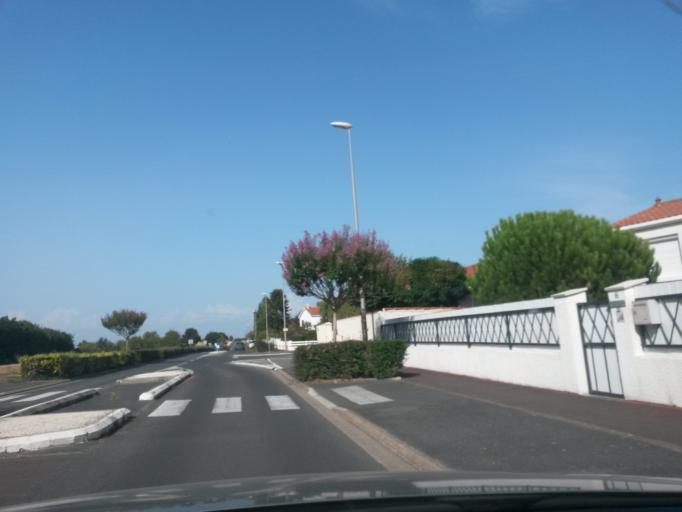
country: FR
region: Poitou-Charentes
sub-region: Departement de la Charente-Maritime
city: Saint-Xandre
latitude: 46.2073
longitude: -1.0993
